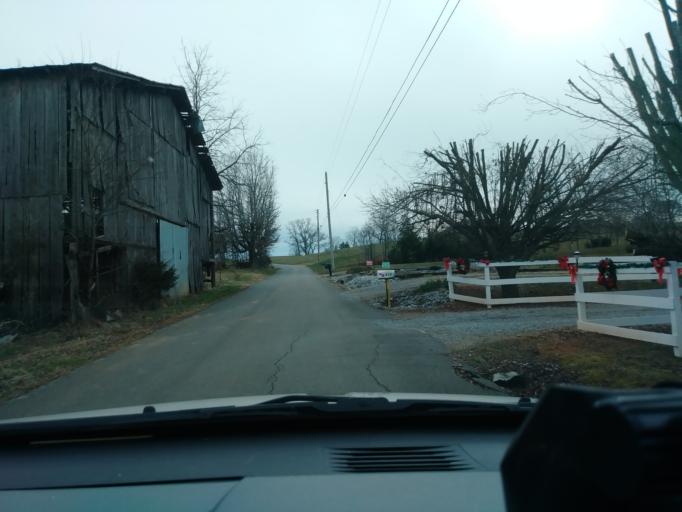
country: US
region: Tennessee
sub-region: Greene County
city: Greeneville
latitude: 36.0877
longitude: -82.8924
